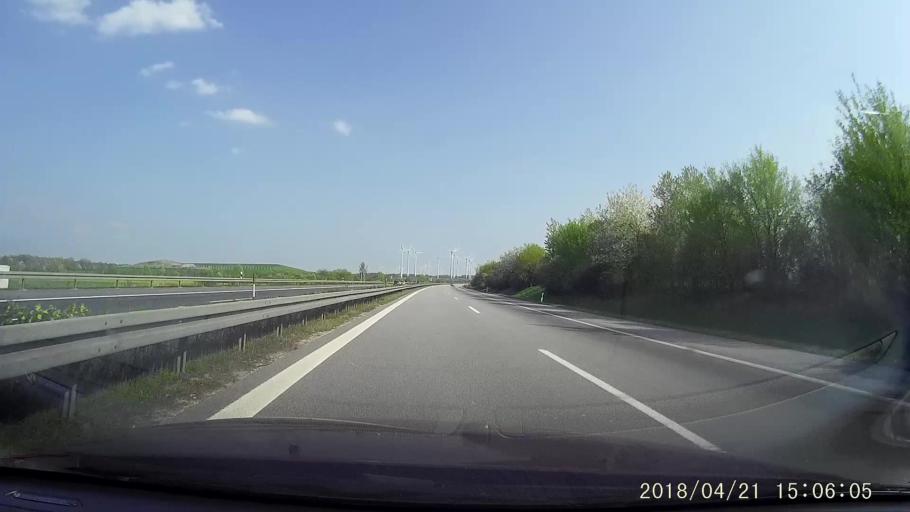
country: DE
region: Saxony
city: Kodersdorf
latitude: 51.2190
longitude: 14.9265
